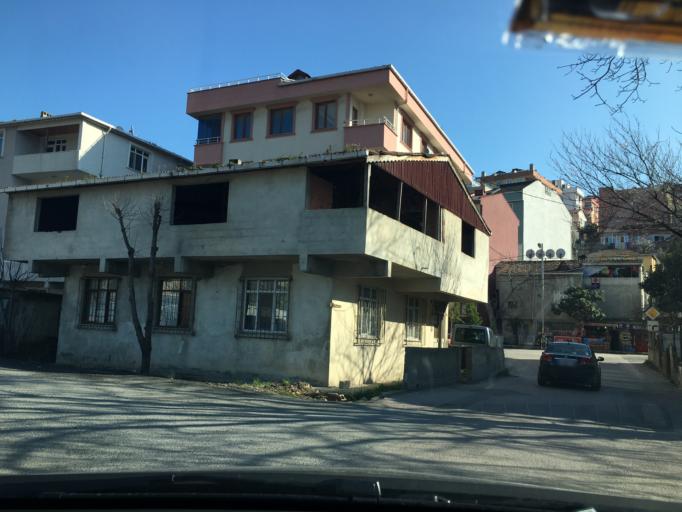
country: TR
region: Istanbul
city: Pendik
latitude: 40.8716
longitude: 29.2891
